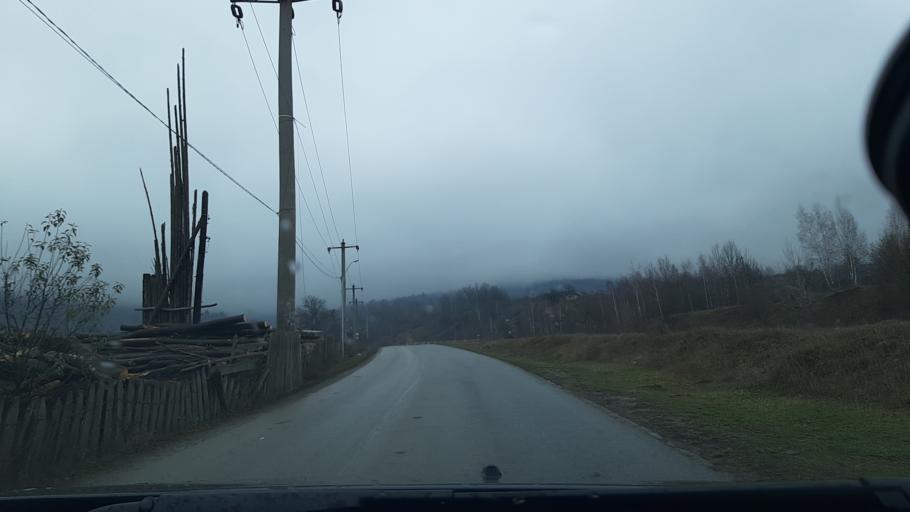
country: RO
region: Hunedoara
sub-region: Oras Petrila
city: Petrila
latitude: 45.4235
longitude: 23.4251
